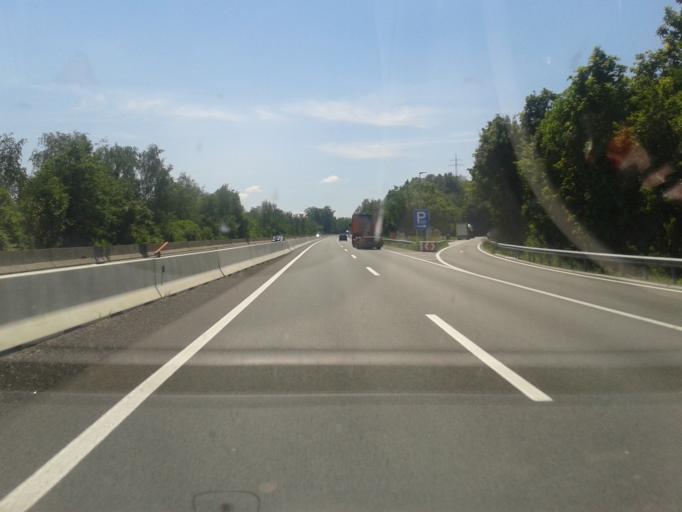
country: AT
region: Carinthia
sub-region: Politischer Bezirk Wolfsberg
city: Sankt Andrae
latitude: 46.7607
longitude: 14.8151
